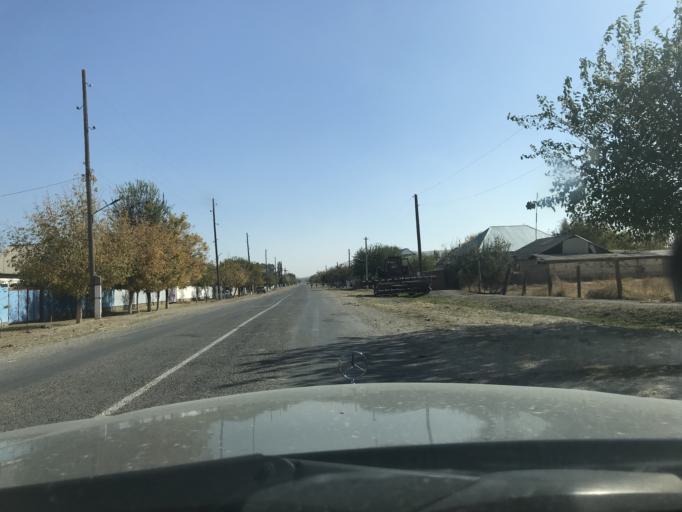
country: KZ
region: Ongtustik Qazaqstan
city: Sastobe
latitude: 42.5464
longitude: 69.9230
